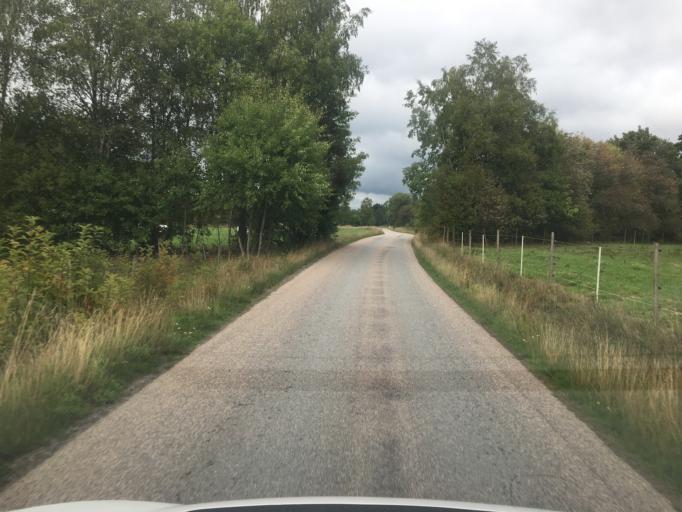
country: SE
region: Kronoberg
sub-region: Ljungby Kommun
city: Lagan
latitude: 56.9225
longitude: 14.0151
